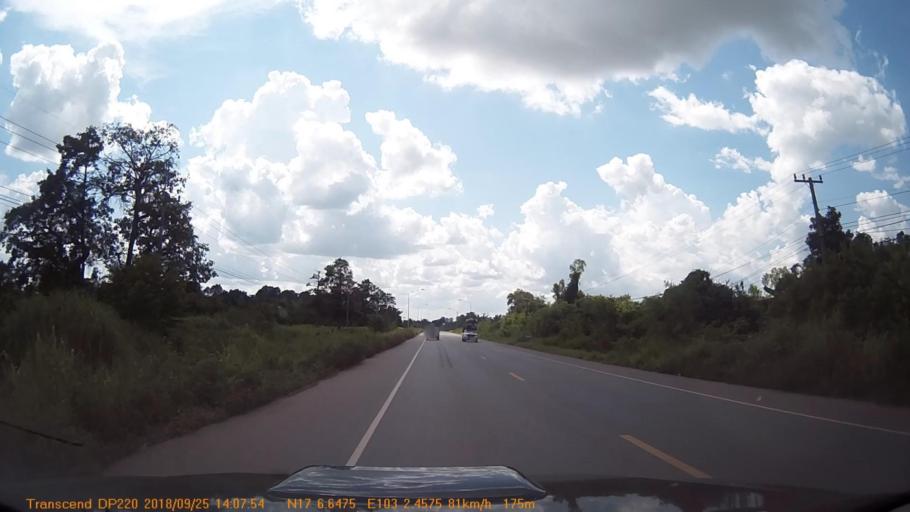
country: TH
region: Changwat Udon Thani
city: Kumphawapi
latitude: 17.1108
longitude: 103.0407
